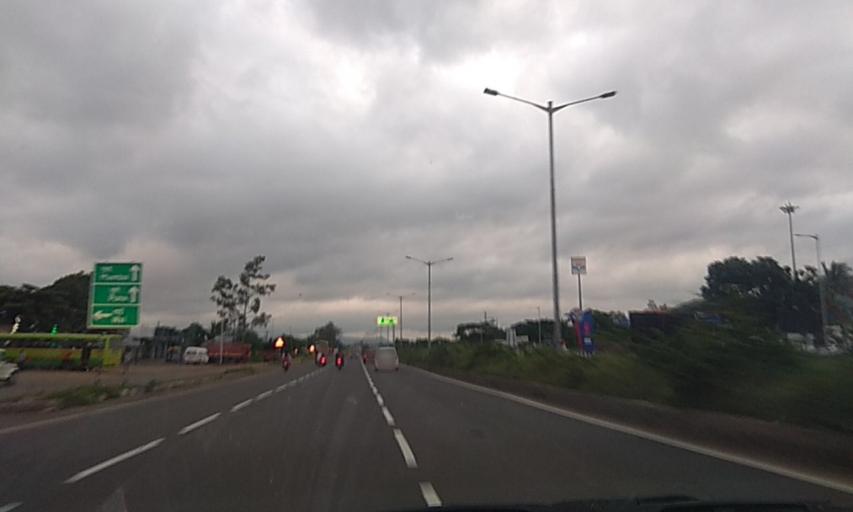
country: IN
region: Maharashtra
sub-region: Satara Division
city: Wai
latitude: 17.8976
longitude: 73.9715
